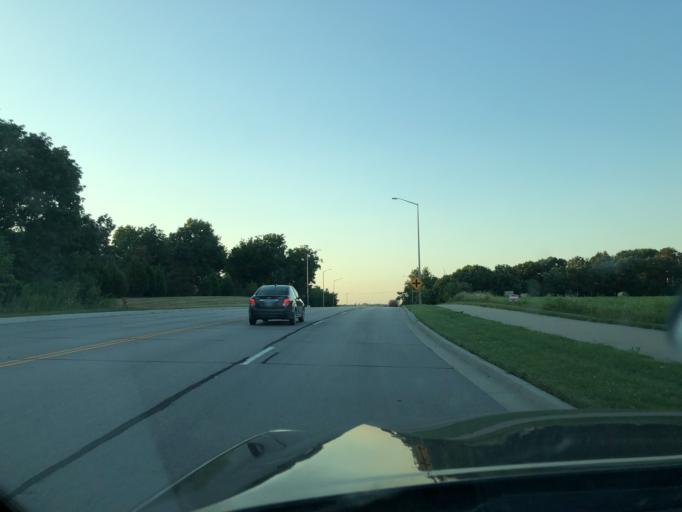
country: US
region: Kansas
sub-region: Leavenworth County
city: Leavenworth
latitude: 39.2994
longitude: -94.9525
